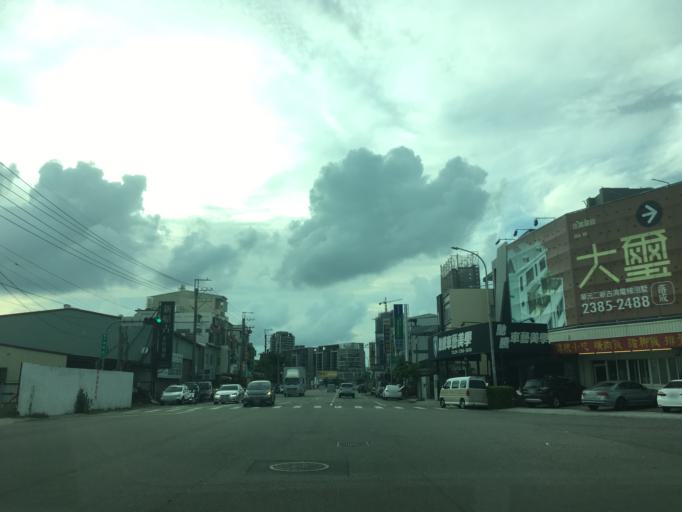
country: TW
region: Taiwan
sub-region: Taichung City
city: Taichung
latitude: 24.1375
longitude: 120.6327
